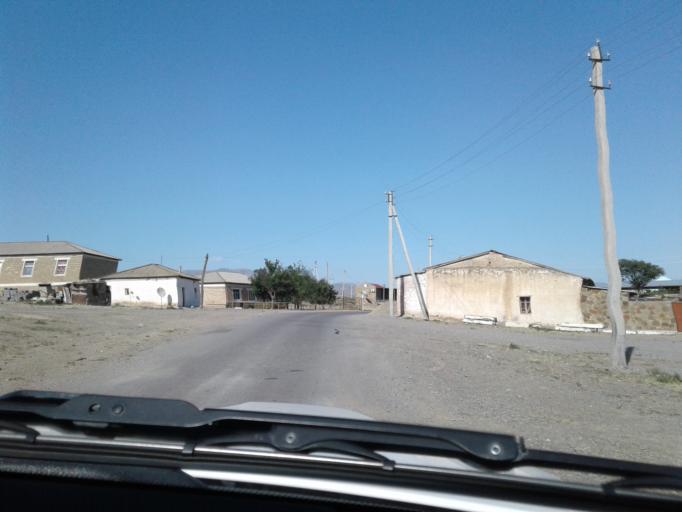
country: TM
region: Balkan
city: Serdar
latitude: 38.7136
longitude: 56.3339
